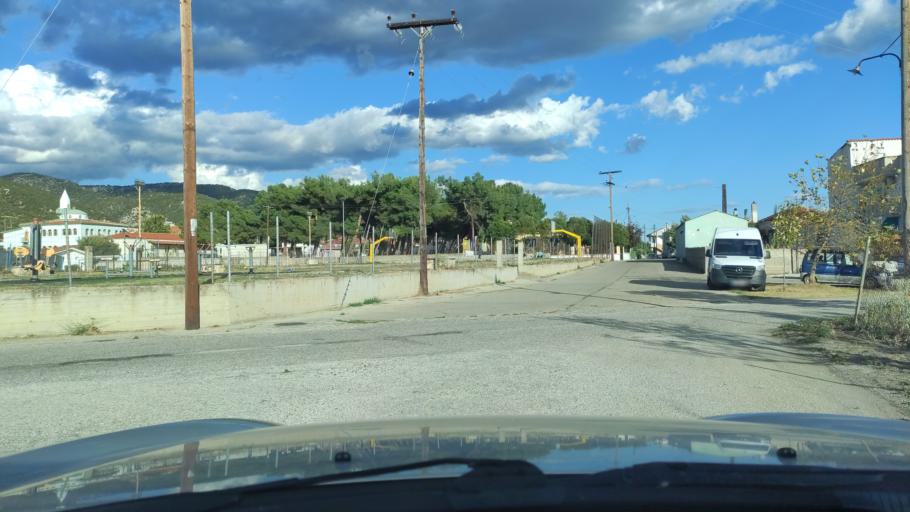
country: GR
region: East Macedonia and Thrace
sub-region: Nomos Xanthis
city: Selero
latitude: 41.1255
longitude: 25.0637
